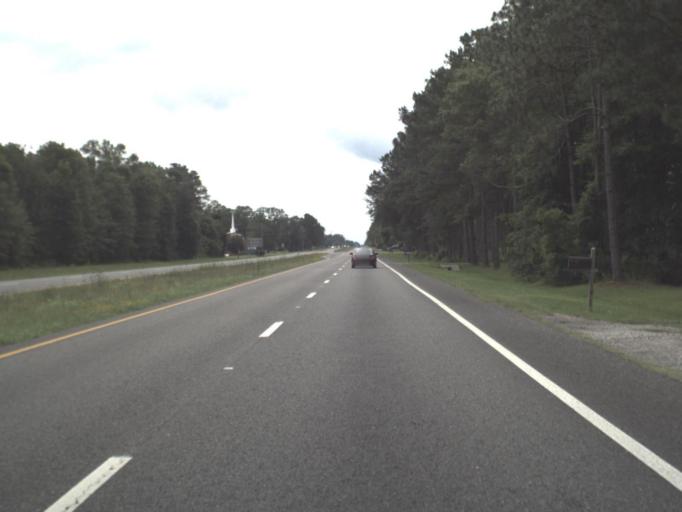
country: US
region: Florida
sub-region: Nassau County
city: Hilliard
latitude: 30.7321
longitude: -81.9465
